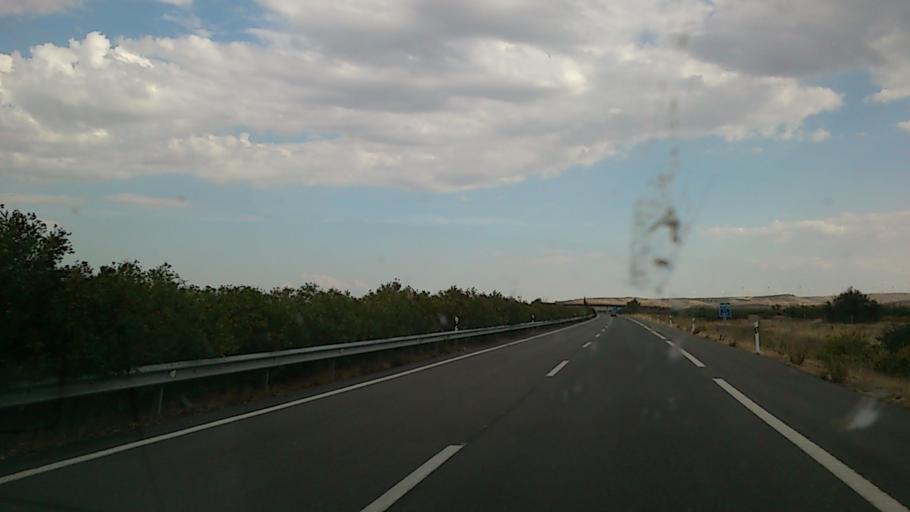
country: ES
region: La Rioja
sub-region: Provincia de La Rioja
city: Pradejon
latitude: 42.3506
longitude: -2.0533
